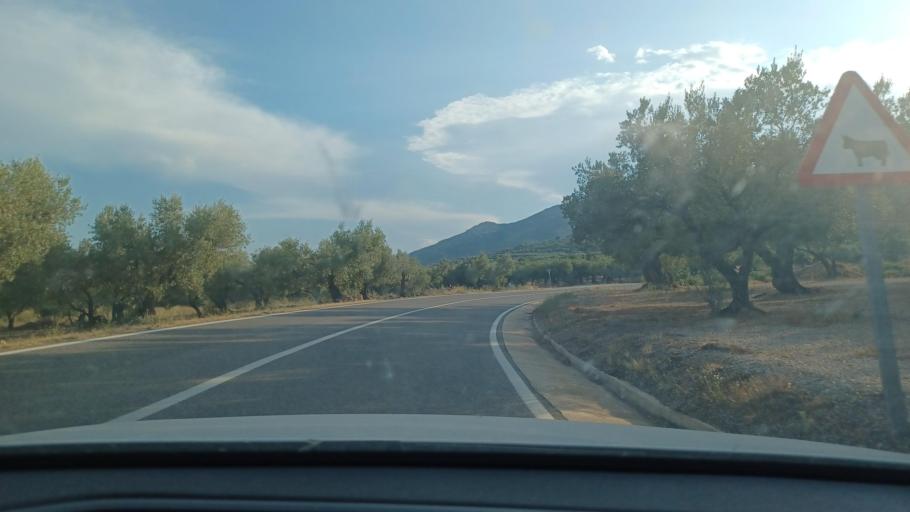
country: ES
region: Catalonia
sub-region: Provincia de Tarragona
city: Mas de Barberans
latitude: 40.7269
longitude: 0.3710
